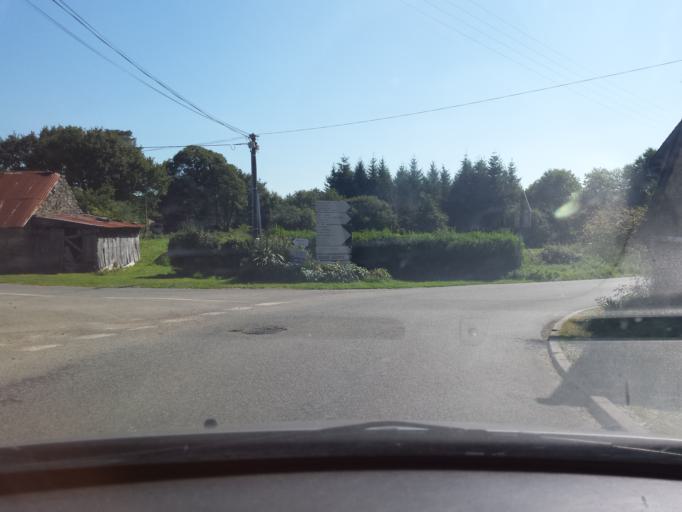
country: FR
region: Brittany
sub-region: Departement des Cotes-d'Armor
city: Plounevez-Quintin
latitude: 48.3320
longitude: -3.2674
